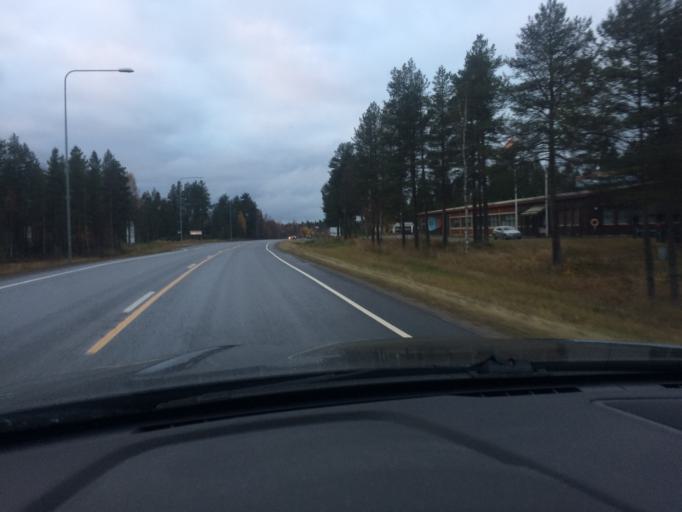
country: FI
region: Northern Ostrobothnia
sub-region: Koillismaa
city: Kuusamo
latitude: 65.9919
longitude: 29.1536
